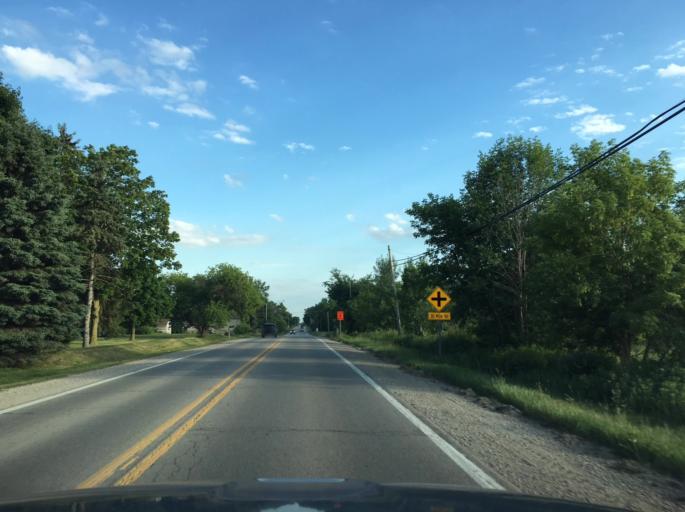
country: US
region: Michigan
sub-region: Macomb County
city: Romeo
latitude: 42.7765
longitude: -82.9616
